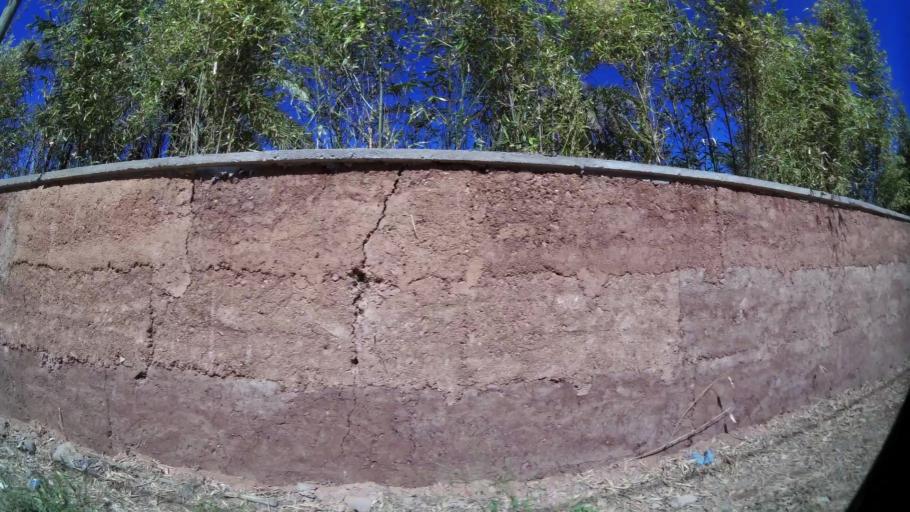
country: MA
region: Marrakech-Tensift-Al Haouz
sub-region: Marrakech
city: Marrakesh
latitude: 31.6677
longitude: -7.9598
